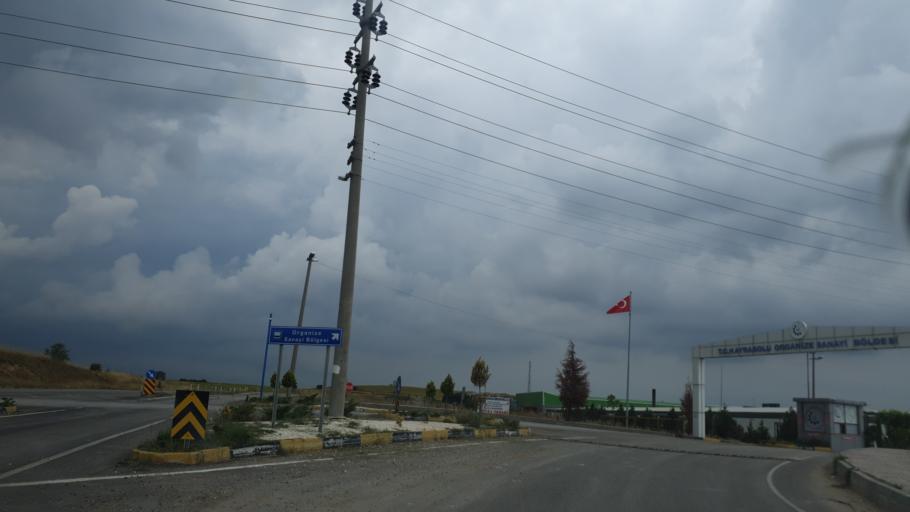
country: TR
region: Tekirdag
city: Hayrabolu
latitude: 41.2218
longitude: 27.0469
